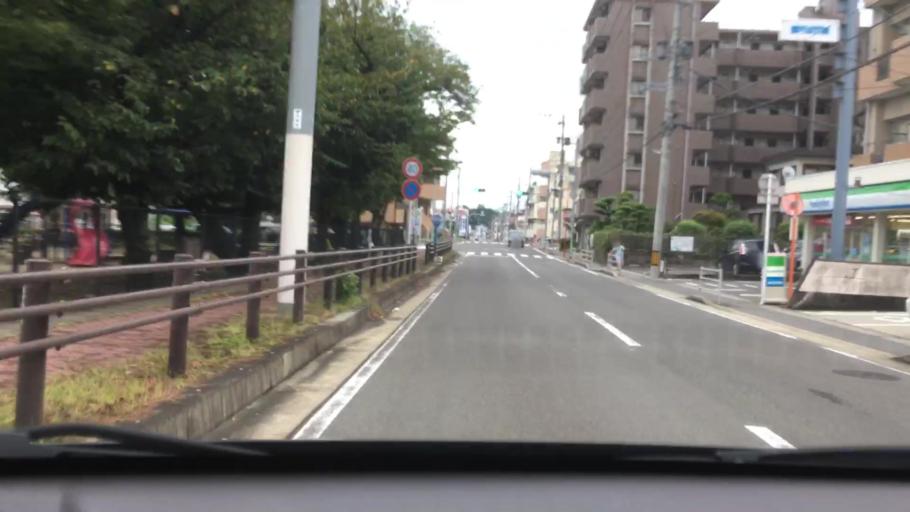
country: JP
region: Nagasaki
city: Nagasaki-shi
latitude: 32.7591
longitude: 129.9421
